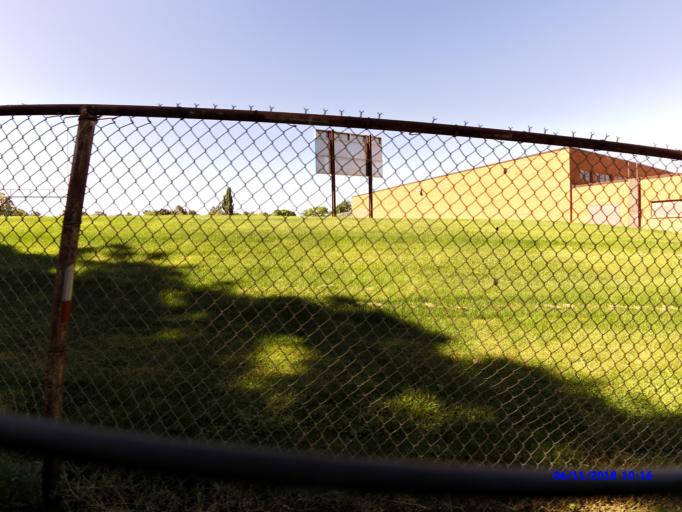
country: US
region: Utah
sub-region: Weber County
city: South Ogden
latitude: 41.2049
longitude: -111.9467
